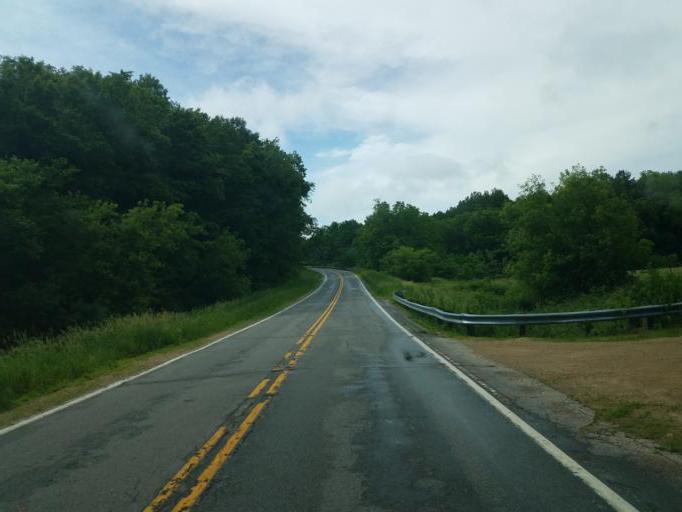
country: US
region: Wisconsin
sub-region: Vernon County
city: Hillsboro
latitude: 43.6636
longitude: -90.4463
